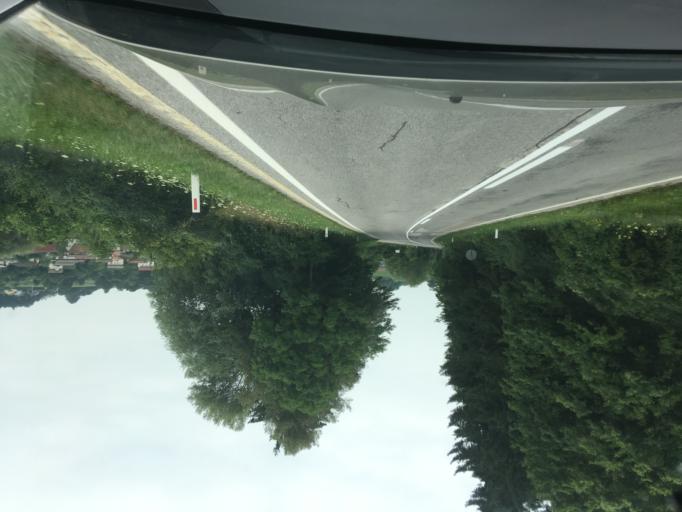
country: SI
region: Skofljica
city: Skofljica
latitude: 45.9837
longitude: 14.5864
